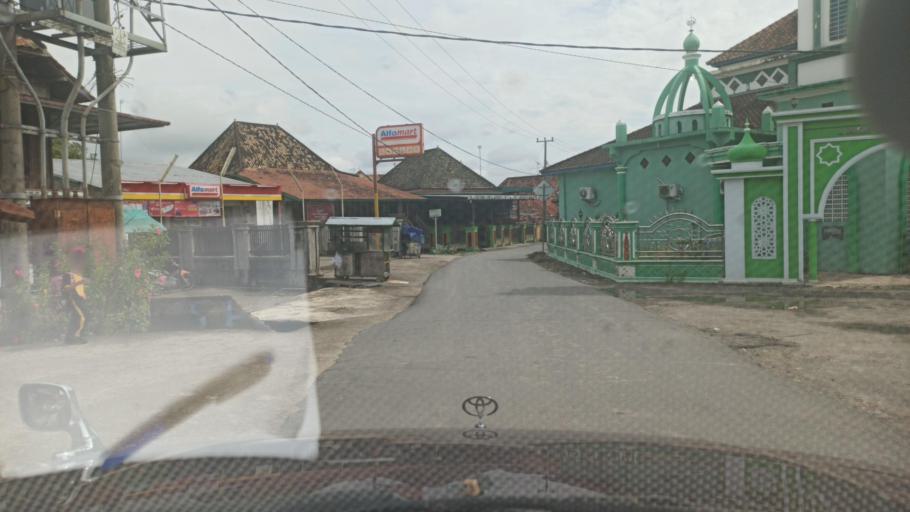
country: ID
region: South Sumatra
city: Gunungmenang
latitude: -3.1108
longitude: 104.0747
